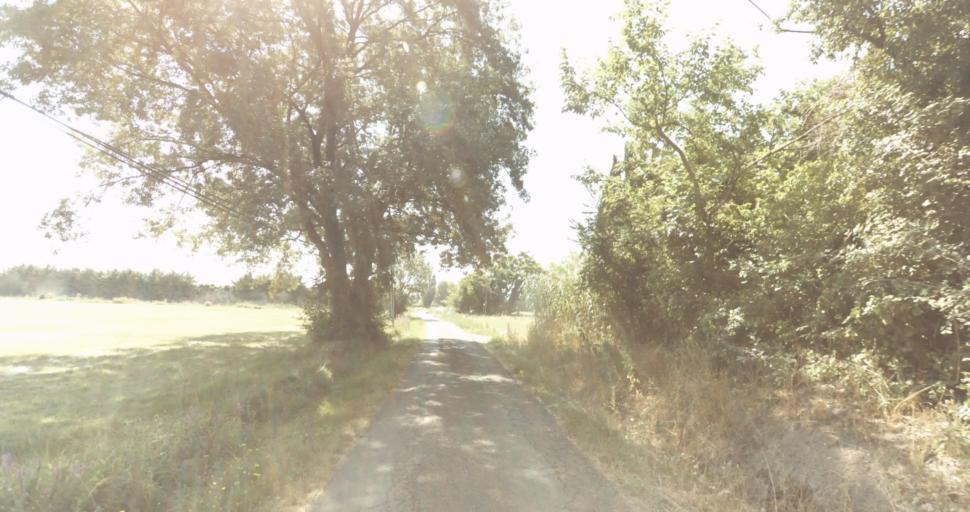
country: FR
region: Provence-Alpes-Cote d'Azur
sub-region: Departement du Vaucluse
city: Monteux
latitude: 44.0202
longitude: 5.0118
